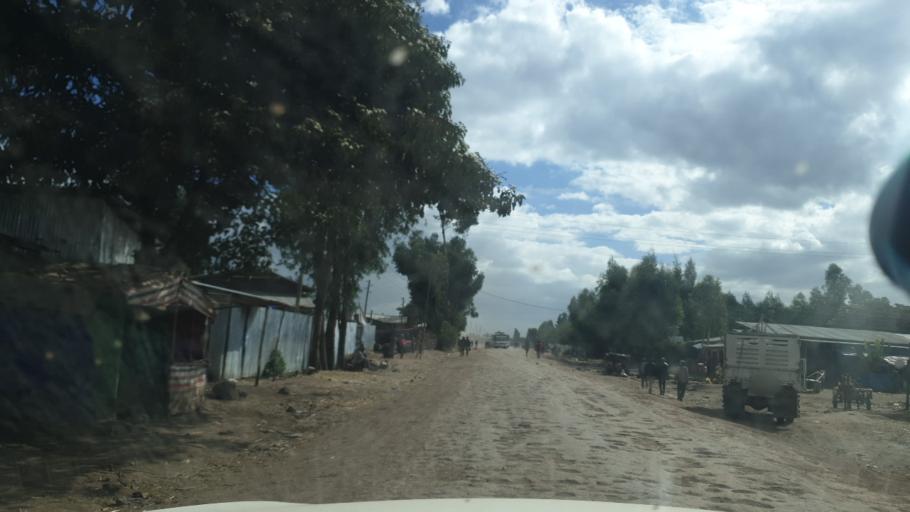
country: ET
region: Oromiya
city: Ziway
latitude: 7.7338
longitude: 39.0325
